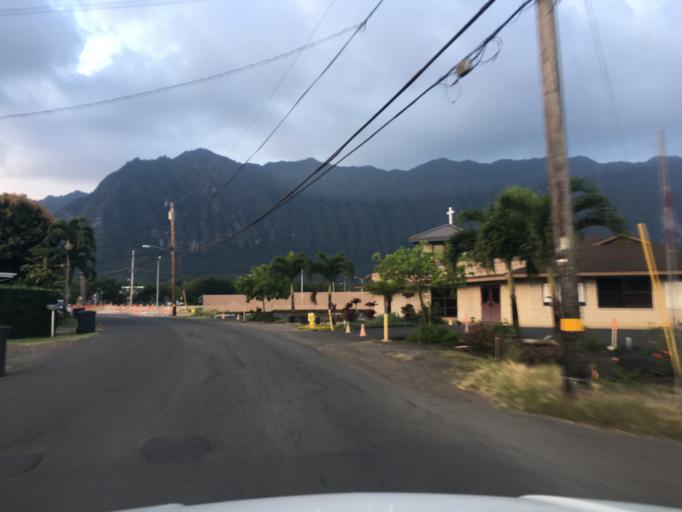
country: US
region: Hawaii
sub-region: Honolulu County
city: Waimanalo
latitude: 21.3463
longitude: -157.7227
